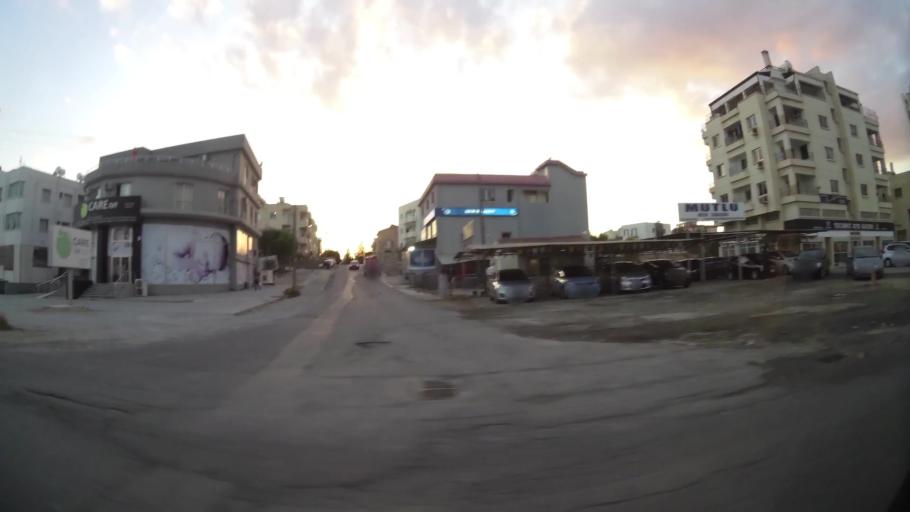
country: CY
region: Lefkosia
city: Nicosia
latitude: 35.2085
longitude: 33.3664
